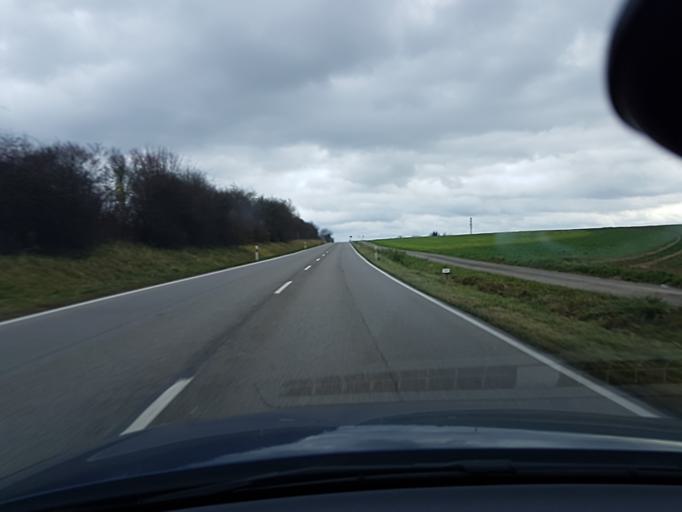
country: DE
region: Baden-Wuerttemberg
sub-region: Regierungsbezirk Stuttgart
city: Aspach
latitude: 48.9706
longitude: 9.3868
